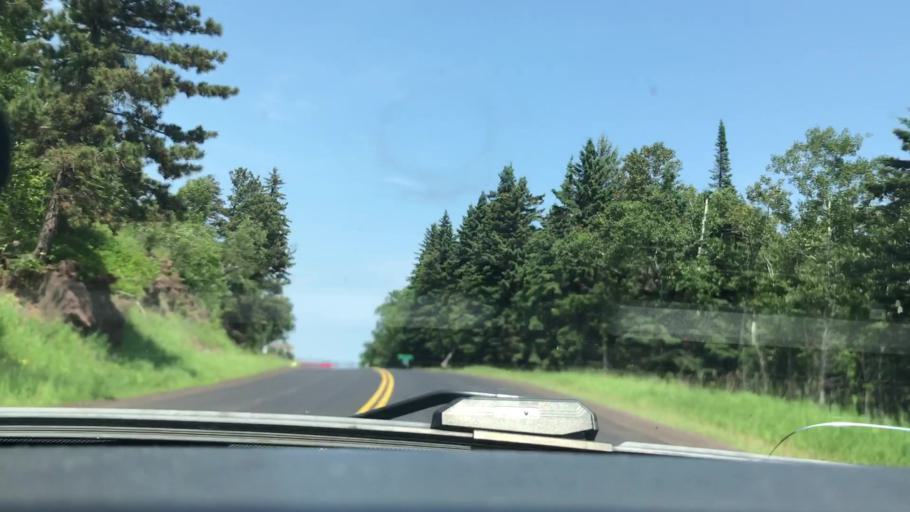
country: US
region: Minnesota
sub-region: Lake County
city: Silver Bay
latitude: 47.2698
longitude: -91.2816
